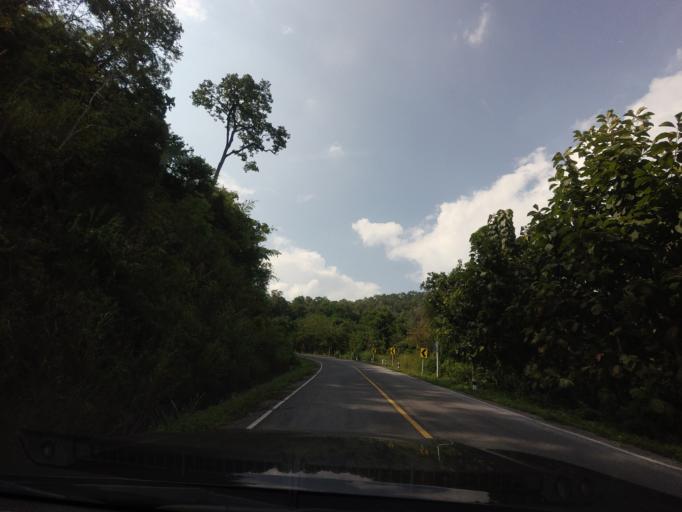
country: TH
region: Uttaradit
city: Ban Khok
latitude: 18.2417
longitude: 101.0080
